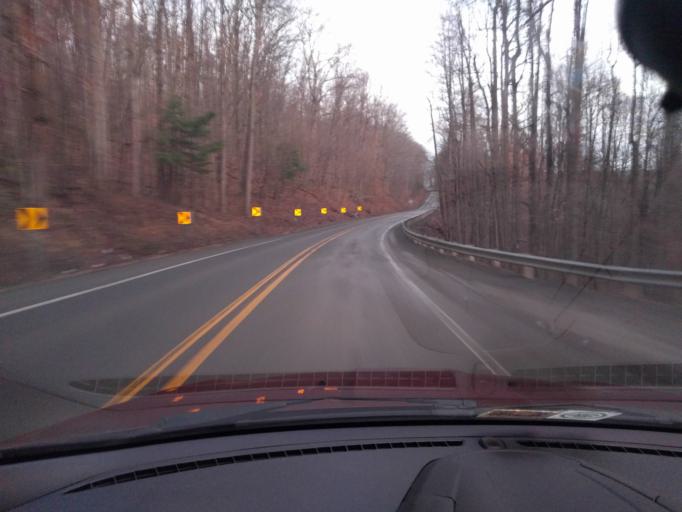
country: US
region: West Virginia
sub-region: Greenbrier County
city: Rainelle
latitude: 37.9876
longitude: -80.8606
